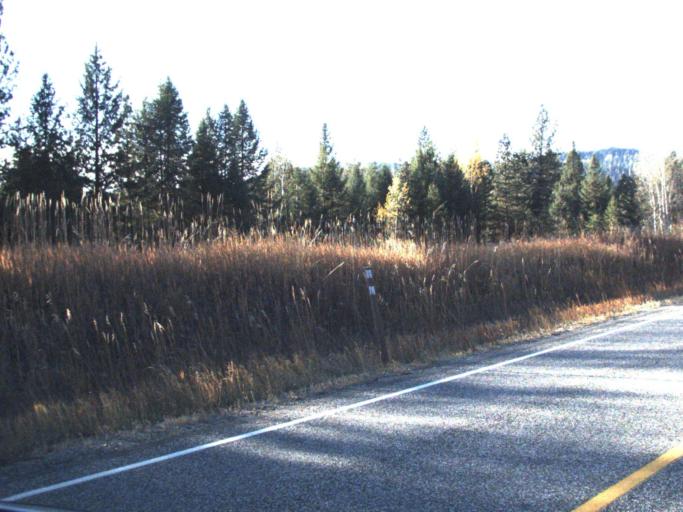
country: CA
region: British Columbia
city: Rossland
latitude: 48.9663
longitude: -117.8076
